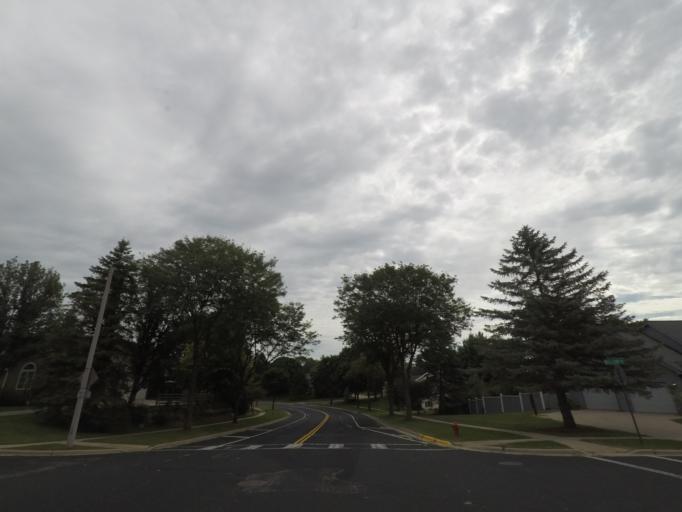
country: US
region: Wisconsin
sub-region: Dane County
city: Middleton
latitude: 43.0872
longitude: -89.4896
